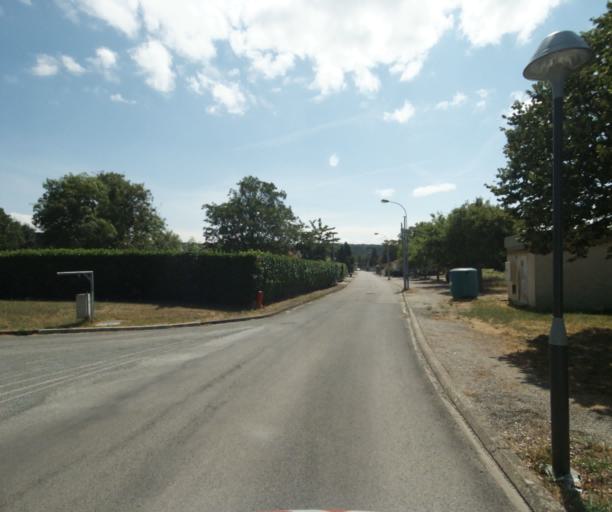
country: FR
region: Midi-Pyrenees
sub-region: Departement de la Haute-Garonne
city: Revel
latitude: 43.4610
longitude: 2.0169
